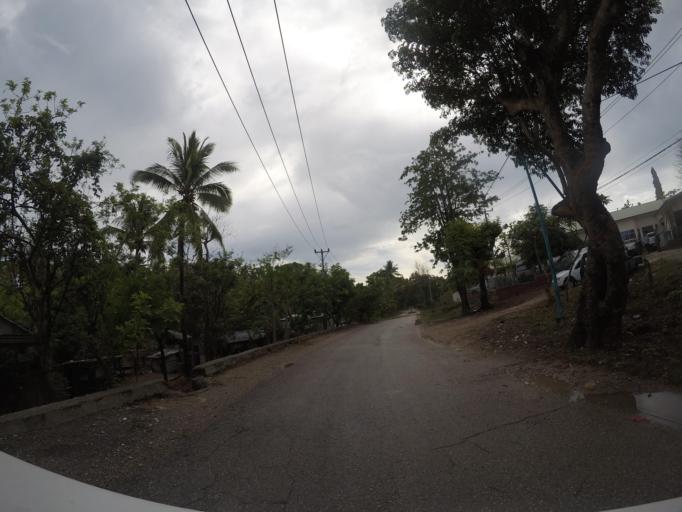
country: TL
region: Baucau
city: Baucau
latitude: -8.4809
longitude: 126.4587
